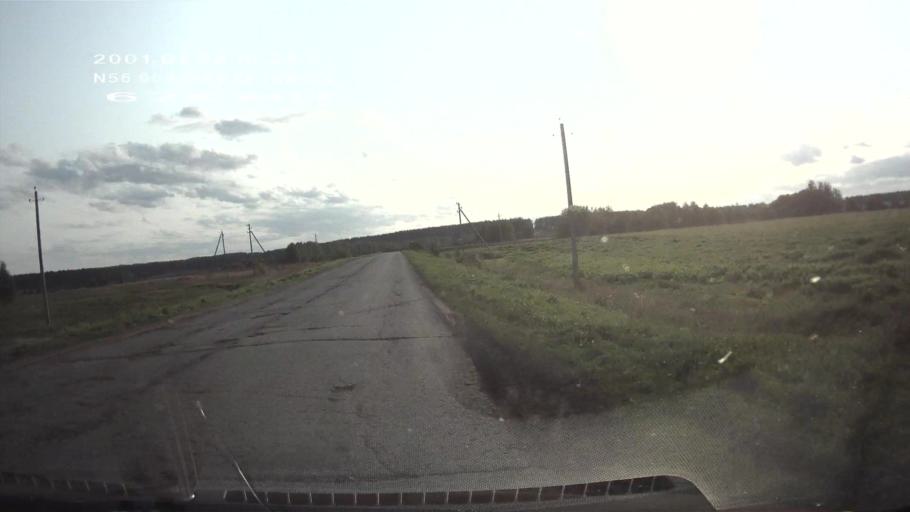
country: RU
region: Mariy-El
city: Kuzhener
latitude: 56.9568
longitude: 48.7671
